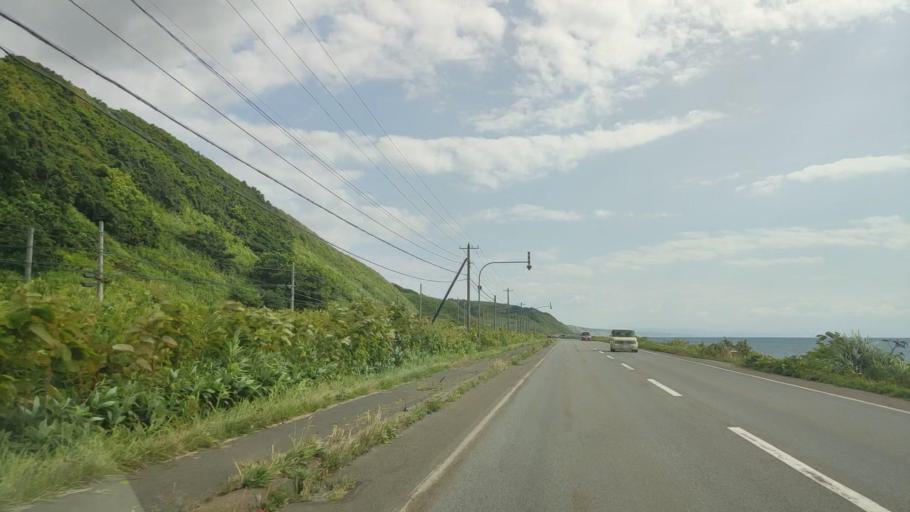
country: JP
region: Hokkaido
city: Rumoi
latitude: 44.1081
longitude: 141.6592
